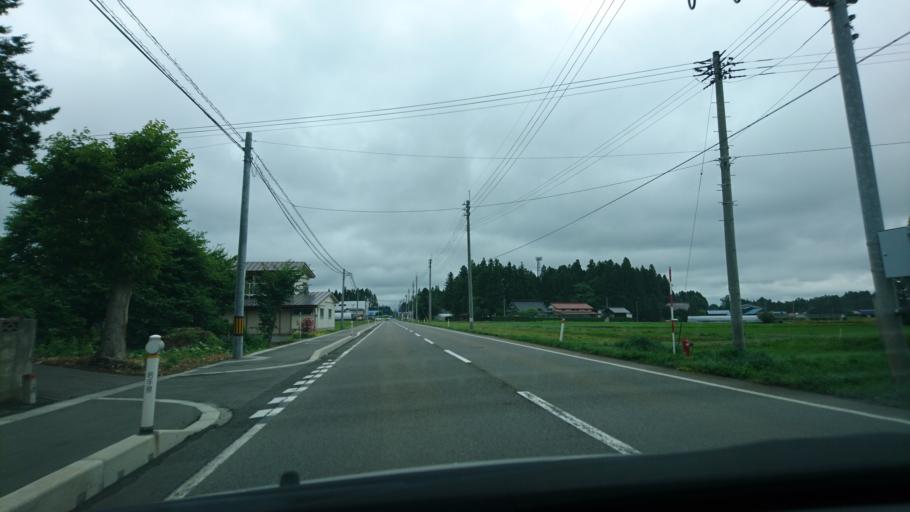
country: JP
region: Iwate
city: Mizusawa
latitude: 39.1043
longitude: 141.0517
